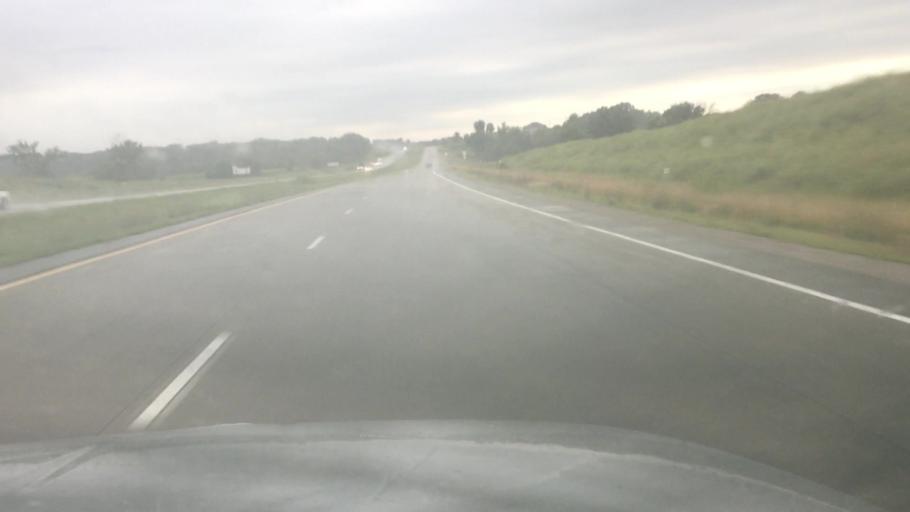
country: US
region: Iowa
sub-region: Washington County
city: Washington
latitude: 41.2848
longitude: -91.5332
